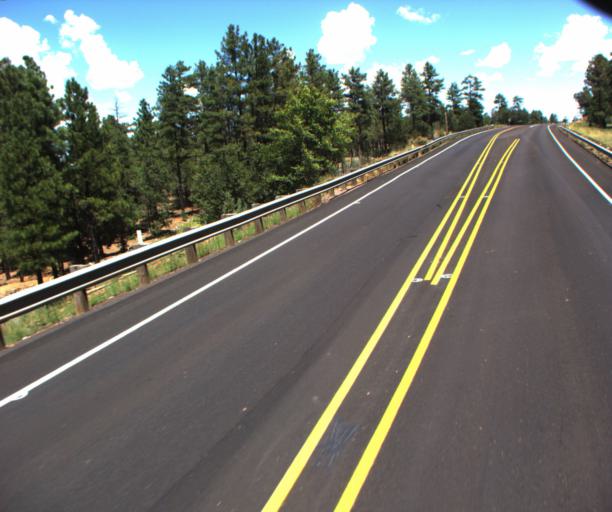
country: US
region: Arizona
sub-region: Navajo County
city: Show Low
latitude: 34.2340
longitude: -110.0654
